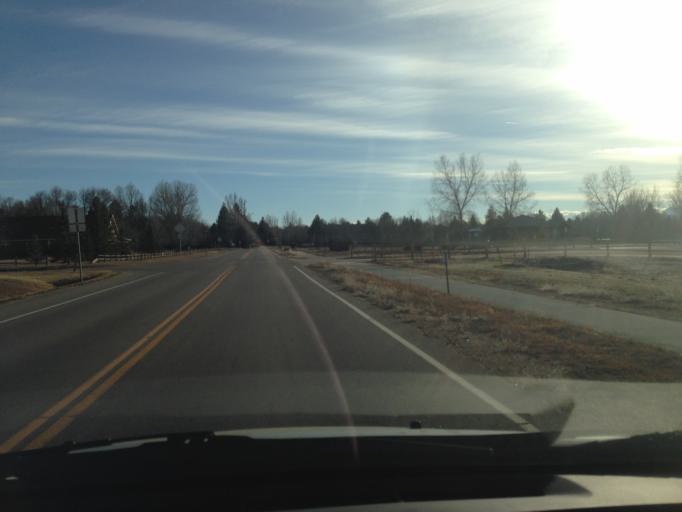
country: US
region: Colorado
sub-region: Boulder County
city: Niwot
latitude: 40.1037
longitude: -105.1595
